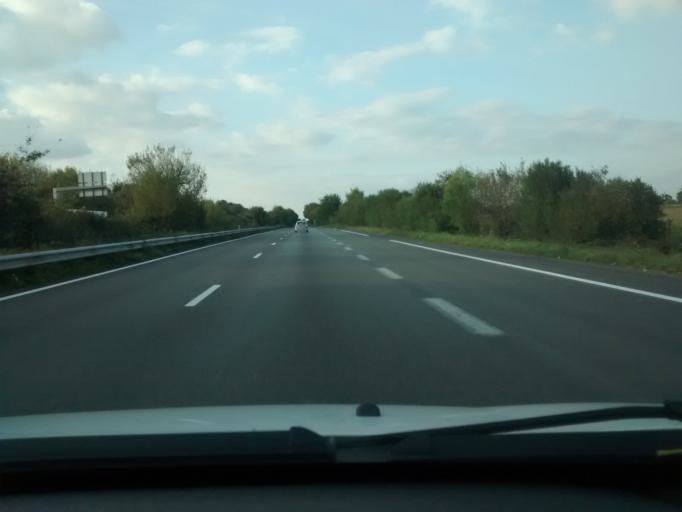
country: FR
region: Pays de la Loire
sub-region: Departement de la Loire-Atlantique
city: Jans
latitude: 47.6287
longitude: -1.6454
